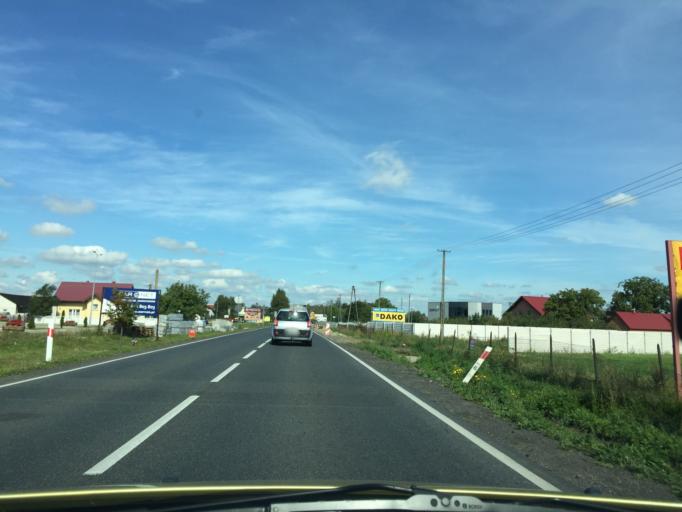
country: PL
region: Greater Poland Voivodeship
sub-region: Kalisz
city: Kalisz
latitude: 51.7977
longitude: 18.0918
